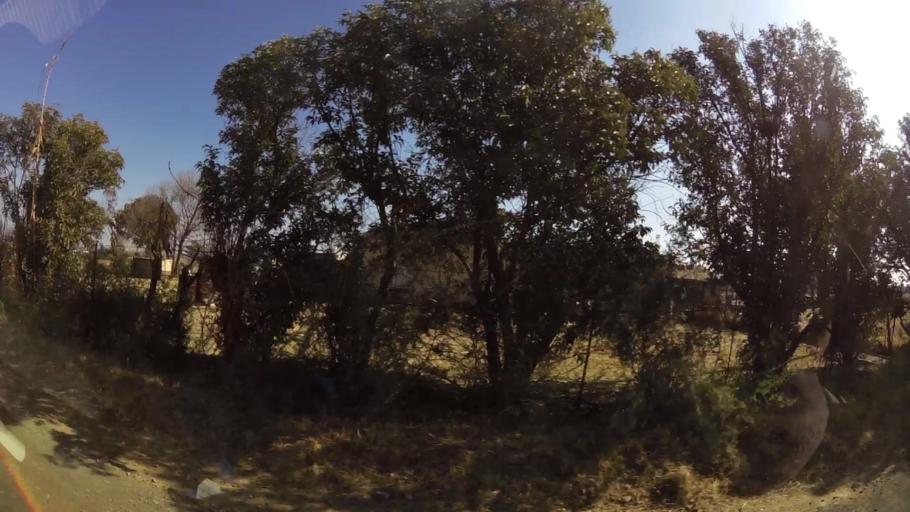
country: ZA
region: Orange Free State
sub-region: Mangaung Metropolitan Municipality
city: Bloemfontein
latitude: -29.1667
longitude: 26.3097
